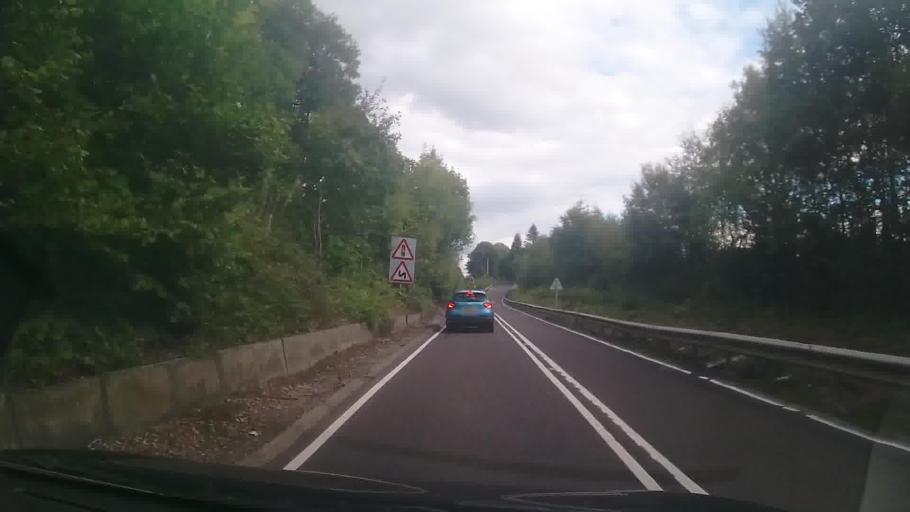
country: GB
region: Scotland
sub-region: Argyll and Bute
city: Garelochhead
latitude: 56.3885
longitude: -5.0709
